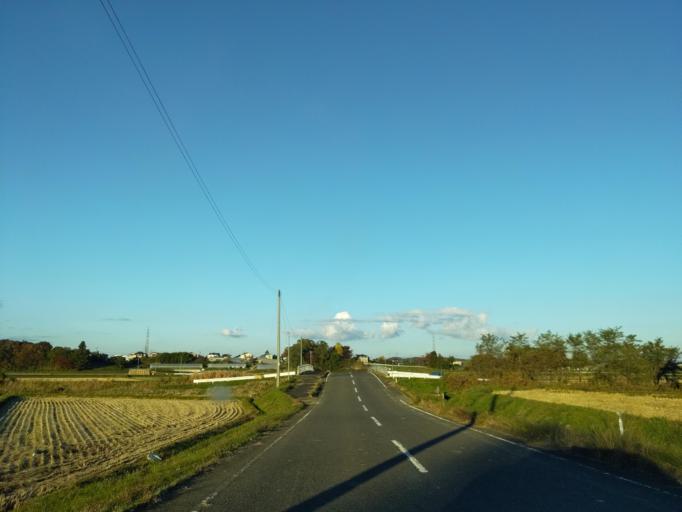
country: JP
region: Fukushima
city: Koriyama
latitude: 37.4505
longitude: 140.3613
